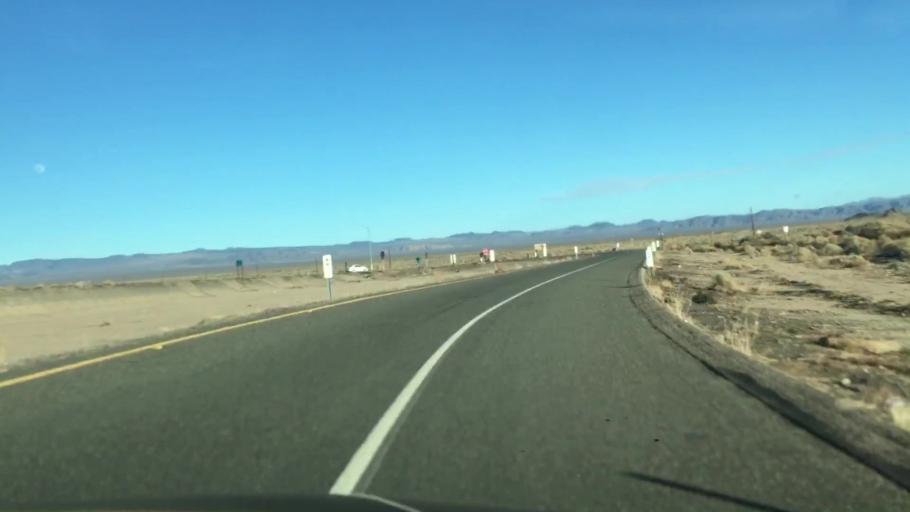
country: US
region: California
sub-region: San Bernardino County
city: Fort Irwin
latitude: 35.2619
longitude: -116.0737
